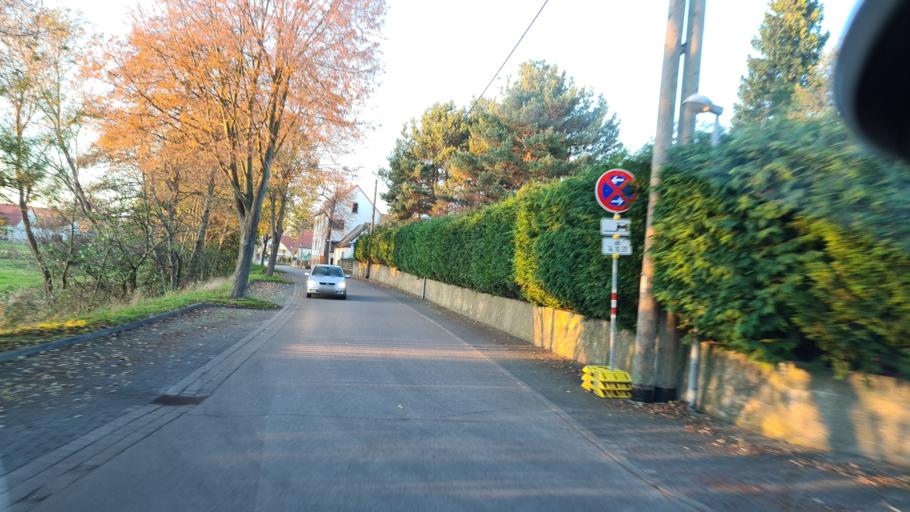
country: DE
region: Saxony
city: Schildau
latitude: 51.4418
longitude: 12.9706
